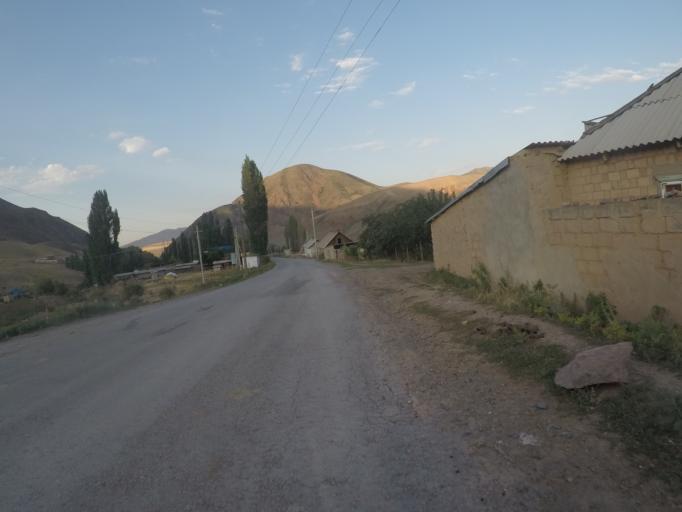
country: KG
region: Chuy
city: Bishkek
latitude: 42.6712
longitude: 74.6479
